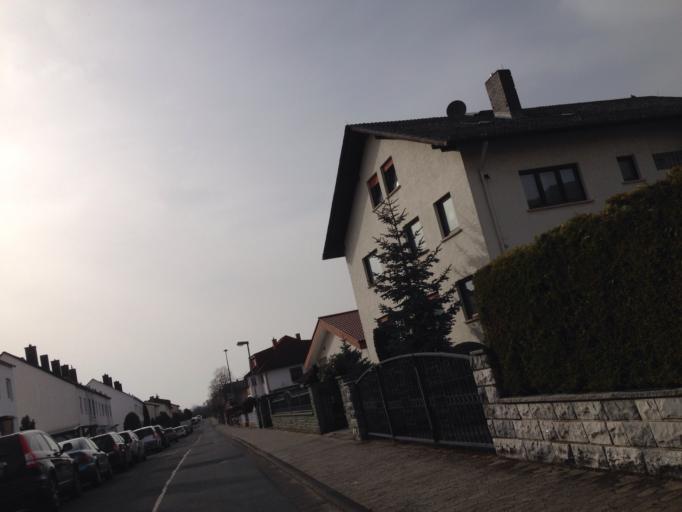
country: DE
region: Hesse
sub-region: Regierungsbezirk Giessen
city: Grossen Buseck
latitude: 50.6035
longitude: 8.7790
